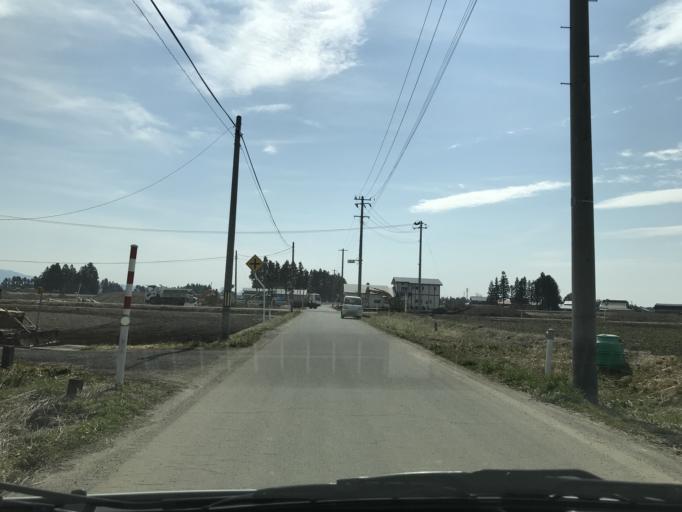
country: JP
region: Iwate
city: Mizusawa
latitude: 39.1390
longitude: 141.0452
